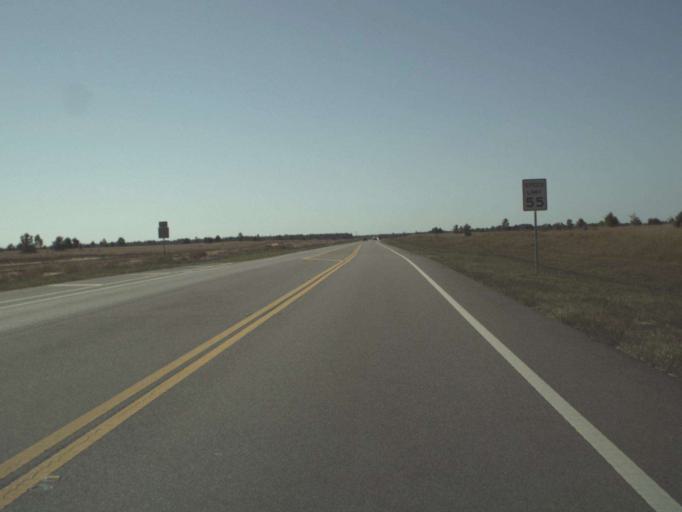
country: US
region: Florida
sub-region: Walton County
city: Freeport
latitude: 30.5506
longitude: -86.1066
